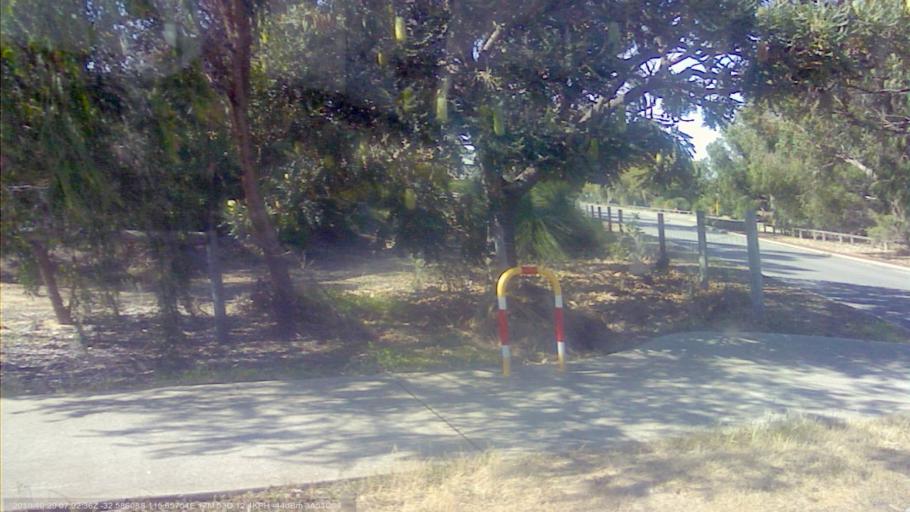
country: AU
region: Western Australia
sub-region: Mandurah
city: Erskine
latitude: -32.5861
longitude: 115.6575
